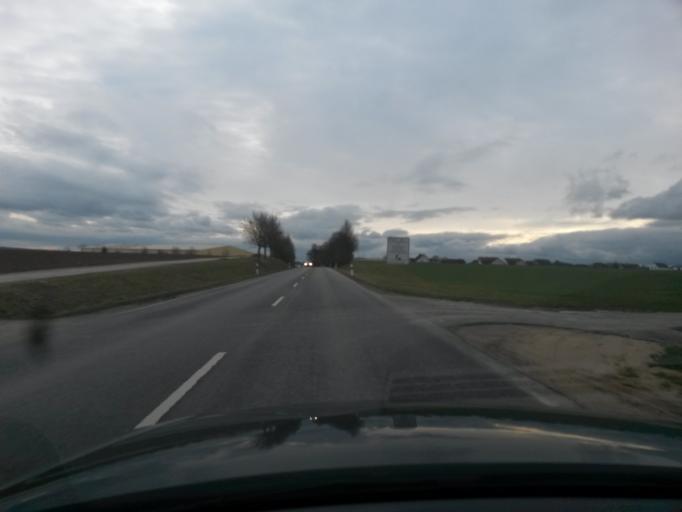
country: DE
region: Bavaria
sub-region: Regierungsbezirk Unterfranken
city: Unterpleichfeld
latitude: 49.8747
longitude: 10.0506
